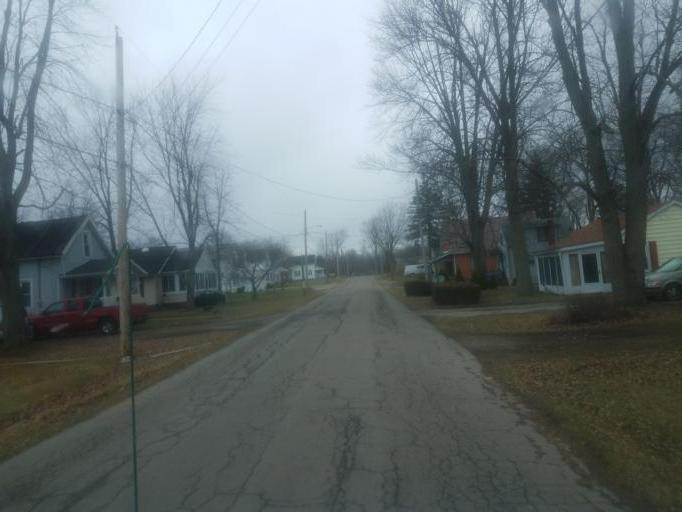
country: US
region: Ohio
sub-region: Crawford County
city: Galion
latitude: 40.7311
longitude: -82.7711
